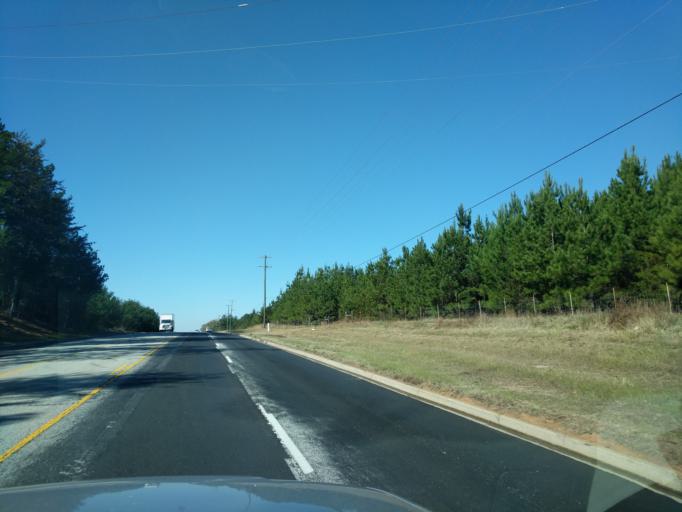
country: US
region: South Carolina
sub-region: Greenville County
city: Greer
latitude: 34.9067
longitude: -82.1977
